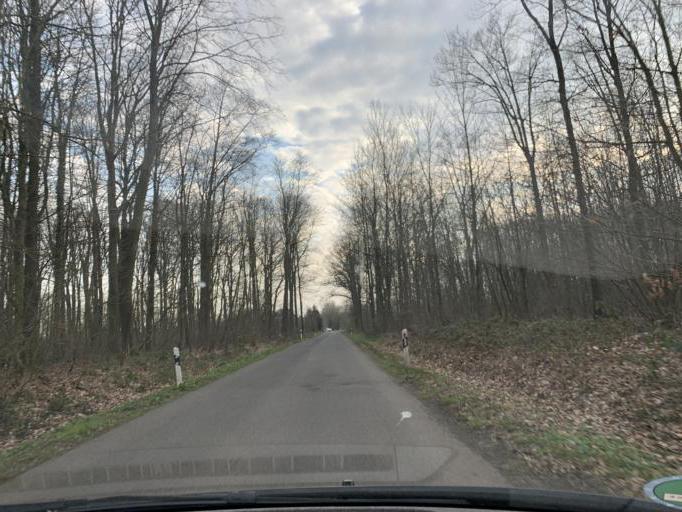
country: DE
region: North Rhine-Westphalia
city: Julich
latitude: 50.9300
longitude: 6.4071
